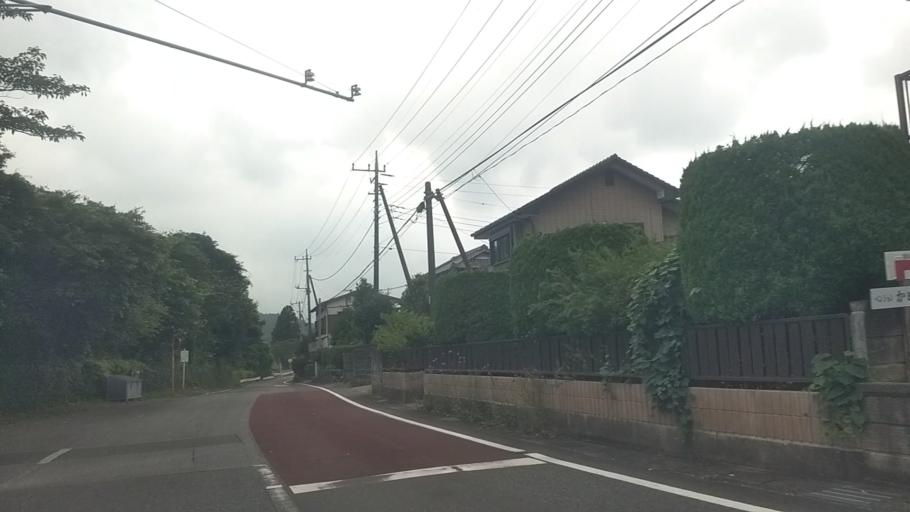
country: JP
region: Chiba
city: Kawaguchi
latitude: 35.2302
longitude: 140.0888
